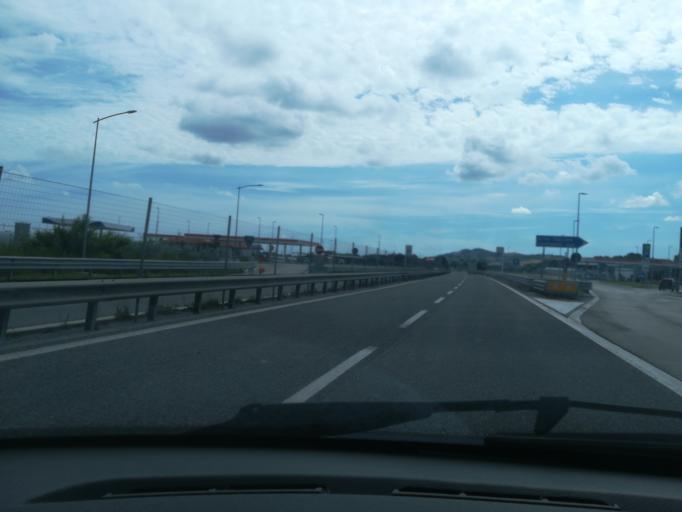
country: IT
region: The Marches
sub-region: Provincia di Macerata
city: Villa San Filippo
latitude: 43.2627
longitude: 13.5607
